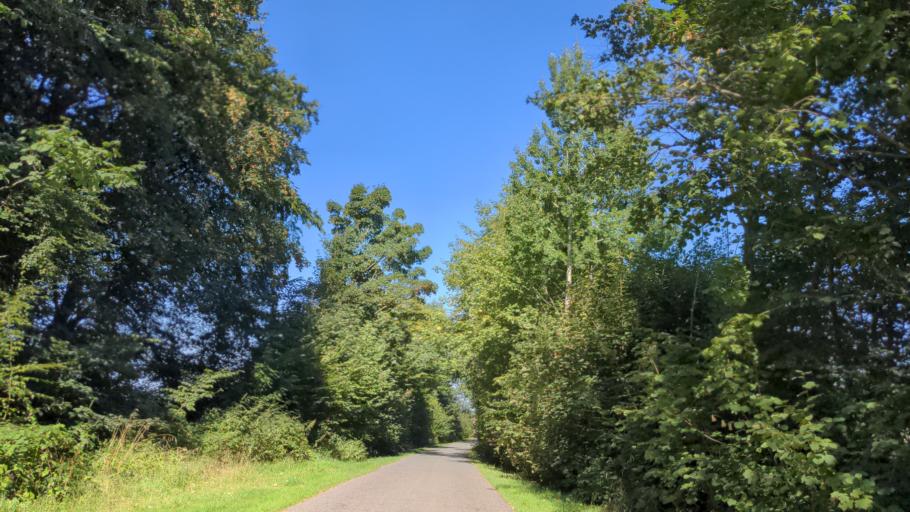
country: DE
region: Schleswig-Holstein
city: Gross Disnack
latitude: 53.7546
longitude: 10.6832
